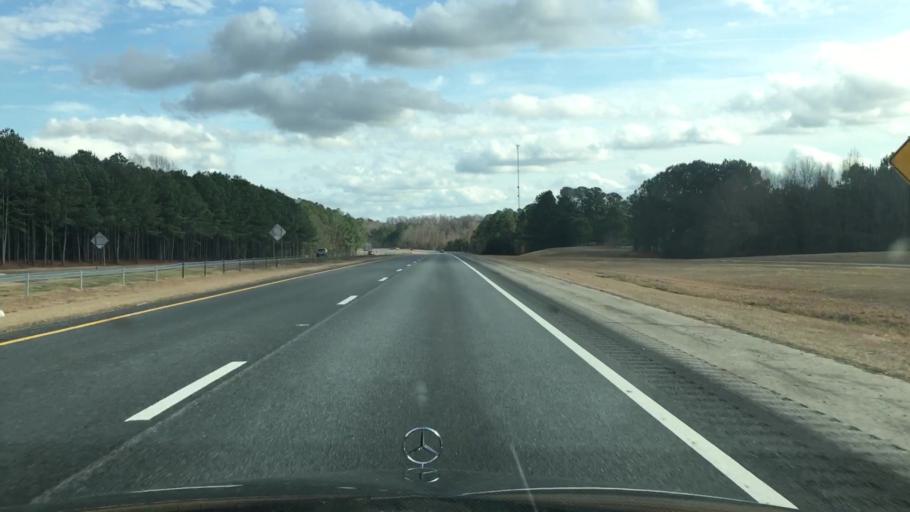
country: US
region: North Carolina
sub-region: Johnston County
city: Benson
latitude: 35.3289
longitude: -78.4473
